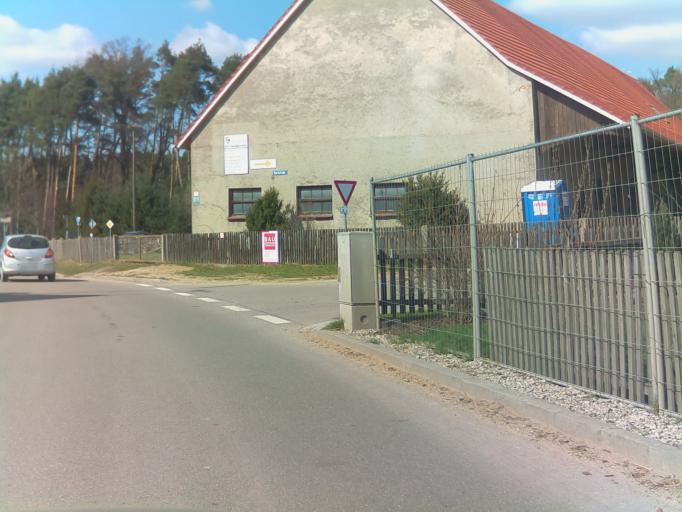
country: DE
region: Bavaria
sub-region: Swabia
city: Kuhbach
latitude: 48.5343
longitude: 11.1683
